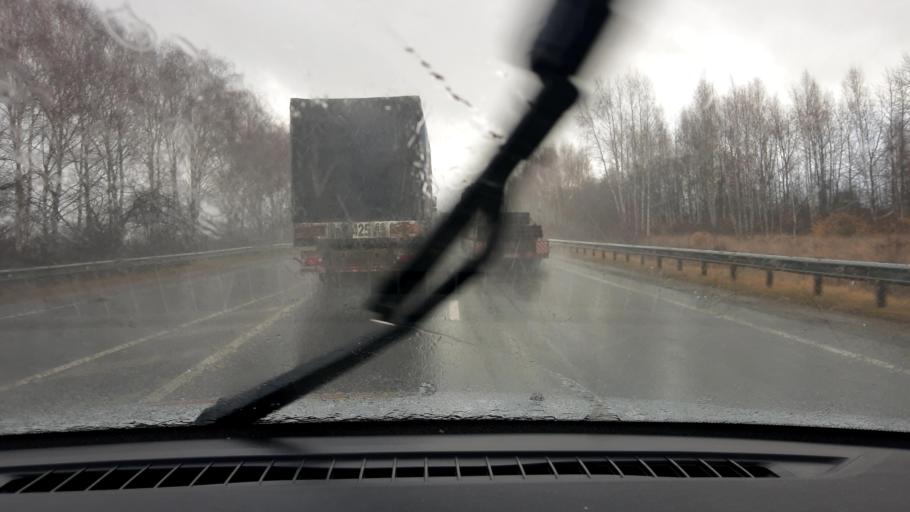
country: RU
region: Nizjnij Novgorod
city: Pamyat' Parizhskoy Kommuny
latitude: 56.0403
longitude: 44.4654
